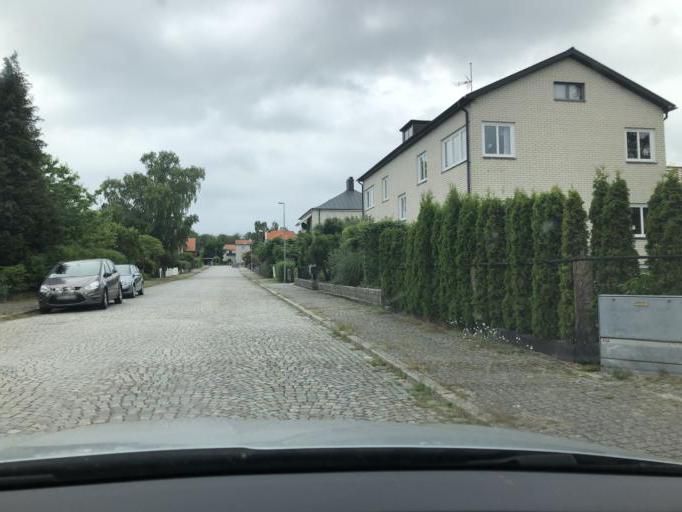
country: SE
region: Blekinge
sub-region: Solvesborgs Kommun
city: Soelvesborg
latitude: 56.0482
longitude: 14.5779
